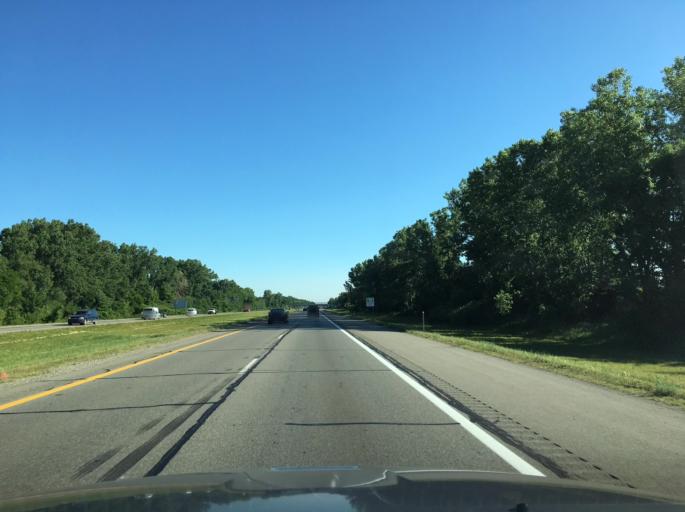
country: US
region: Michigan
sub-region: Macomb County
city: Utica
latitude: 42.6331
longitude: -83.0131
